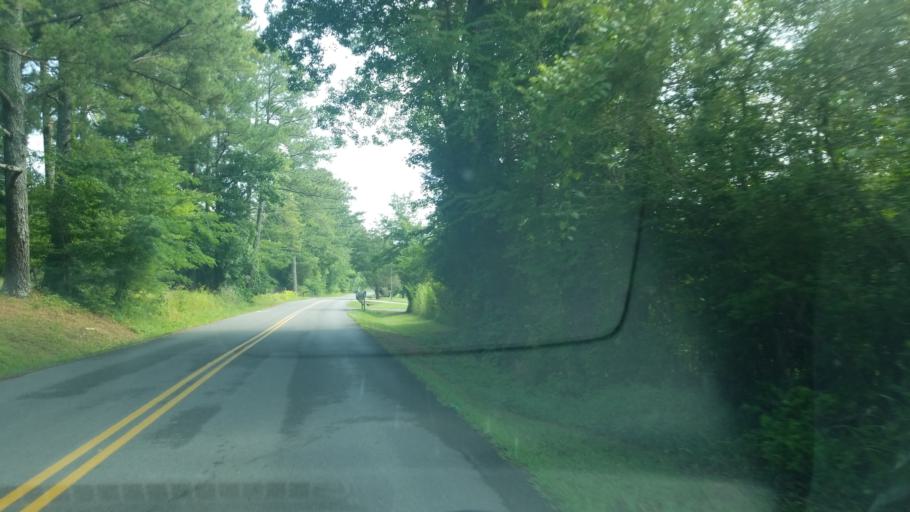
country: US
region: Tennessee
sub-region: Hamilton County
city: Apison
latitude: 35.0803
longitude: -84.9732
